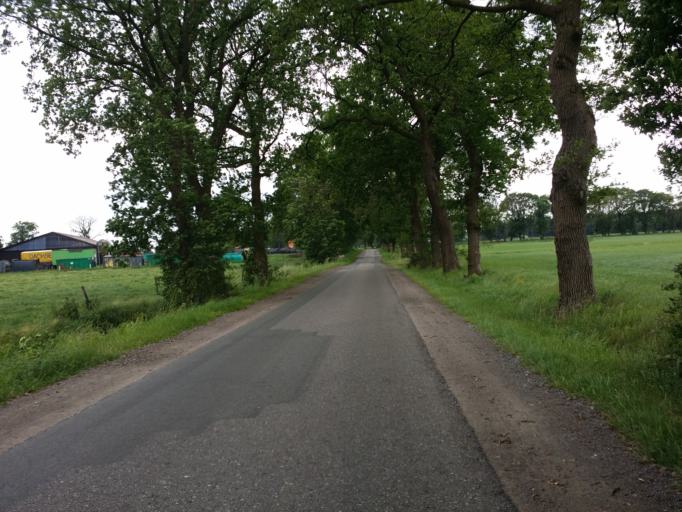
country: DE
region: Lower Saxony
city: Wiefelstede
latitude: 53.3144
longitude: 8.0521
